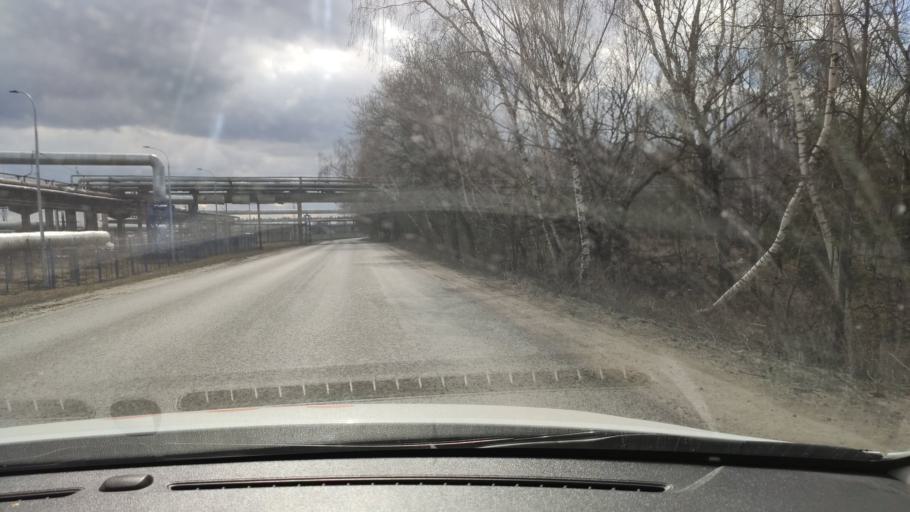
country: RU
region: Tatarstan
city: Staroye Arakchino
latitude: 55.8661
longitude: 48.9721
